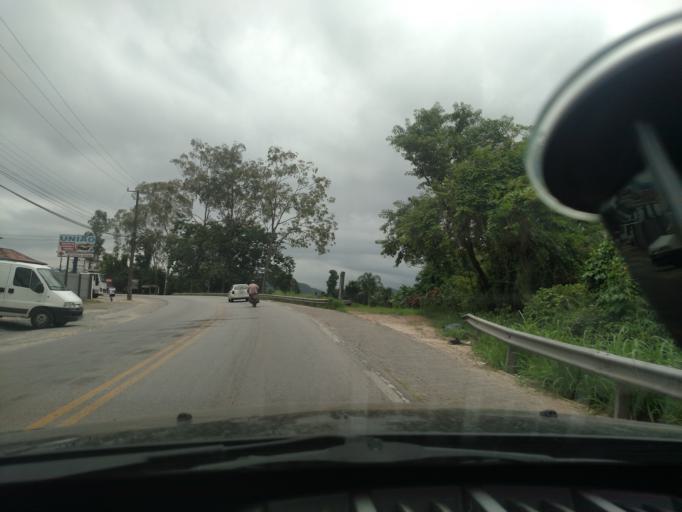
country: BR
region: Santa Catarina
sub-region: Gaspar
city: Gaspar
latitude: -26.9207
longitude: -48.9716
